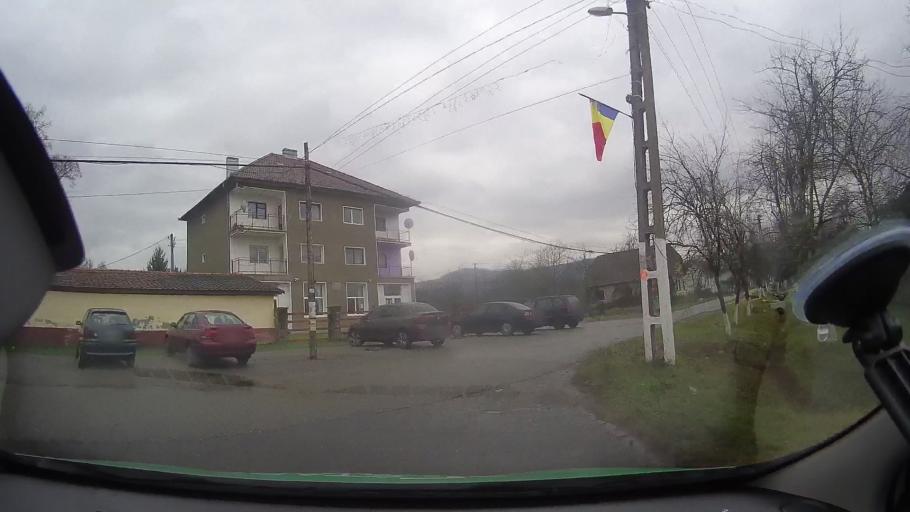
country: RO
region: Arad
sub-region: Comuna Brazii
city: Brazii
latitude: 46.2410
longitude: 22.3343
